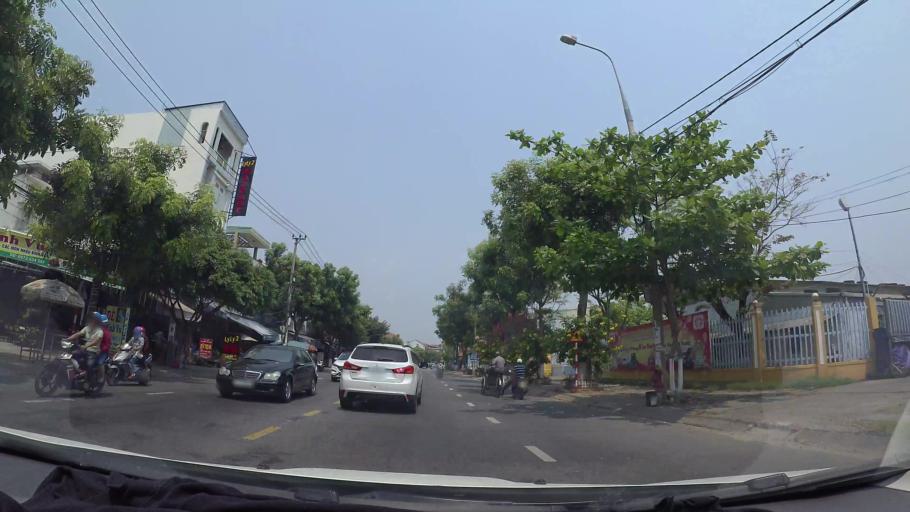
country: VN
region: Da Nang
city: Cam Le
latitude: 16.0012
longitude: 108.2071
